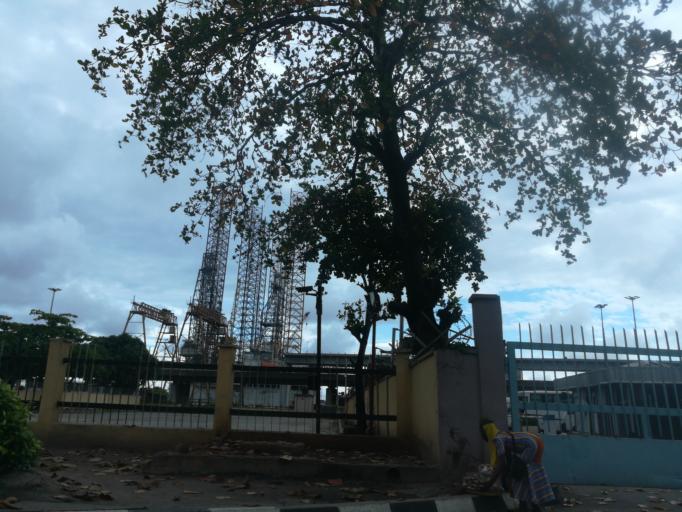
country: NG
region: Lagos
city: Lagos
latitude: 6.4489
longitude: 3.3926
